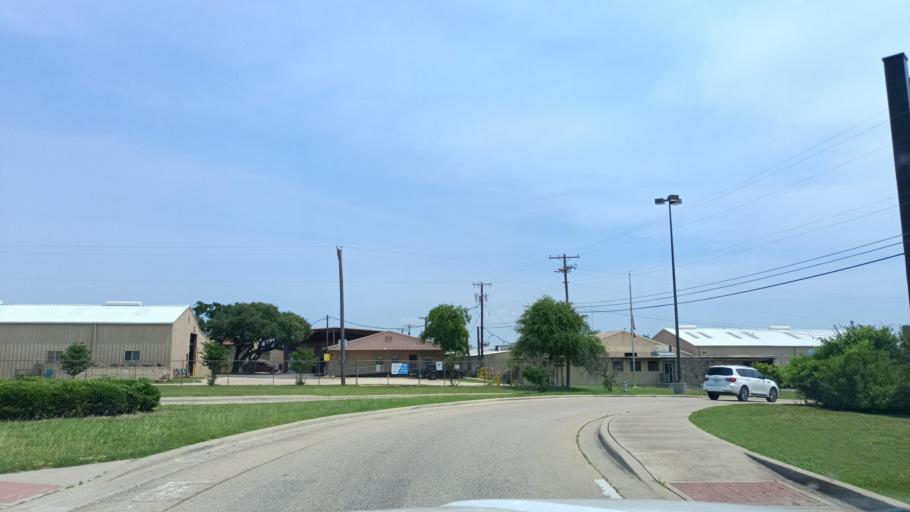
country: US
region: Texas
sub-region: Bell County
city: Temple
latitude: 31.0930
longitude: -97.3874
